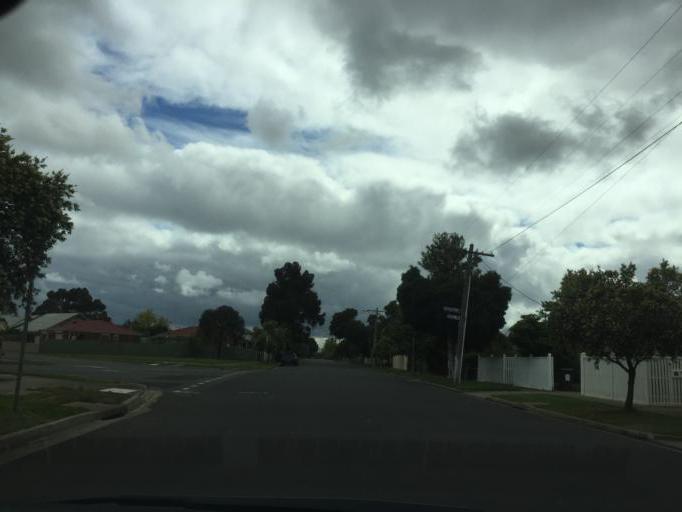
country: AU
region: Victoria
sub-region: Brimbank
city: Sunshine West
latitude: -37.7812
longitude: 144.8226
